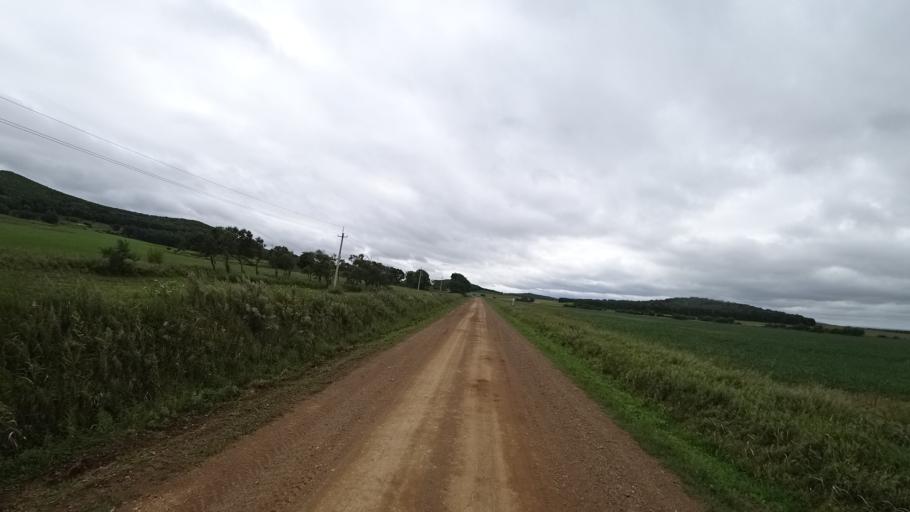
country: RU
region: Primorskiy
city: Chernigovka
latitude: 44.4738
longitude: 132.5805
